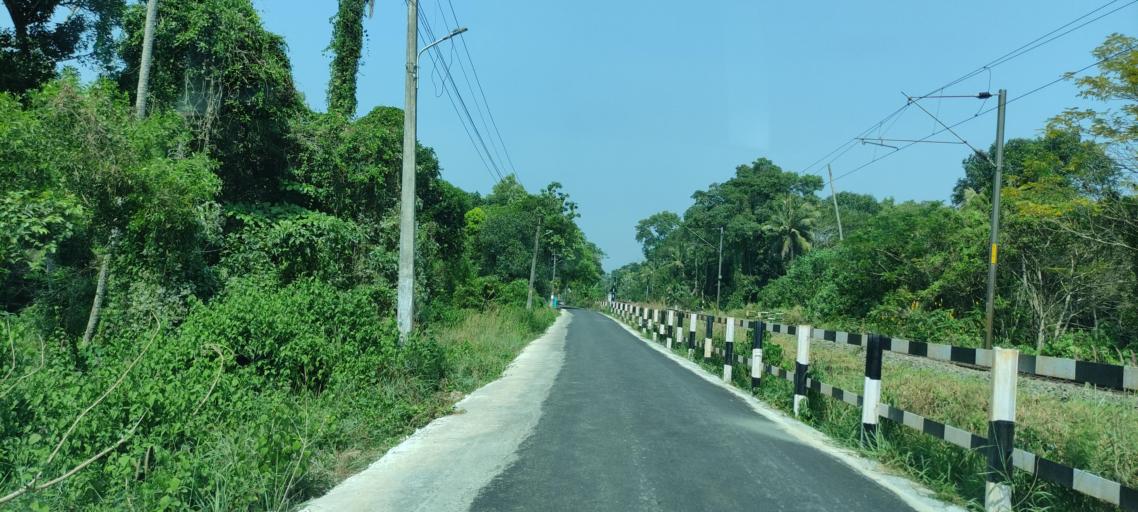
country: IN
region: Kerala
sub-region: Alappuzha
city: Alleppey
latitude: 9.5355
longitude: 76.3210
